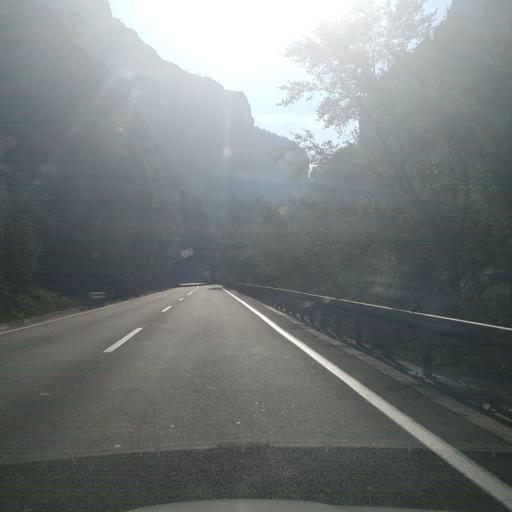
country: RS
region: Central Serbia
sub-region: Nisavski Okrug
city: Svrljig
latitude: 43.3312
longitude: 22.1540
